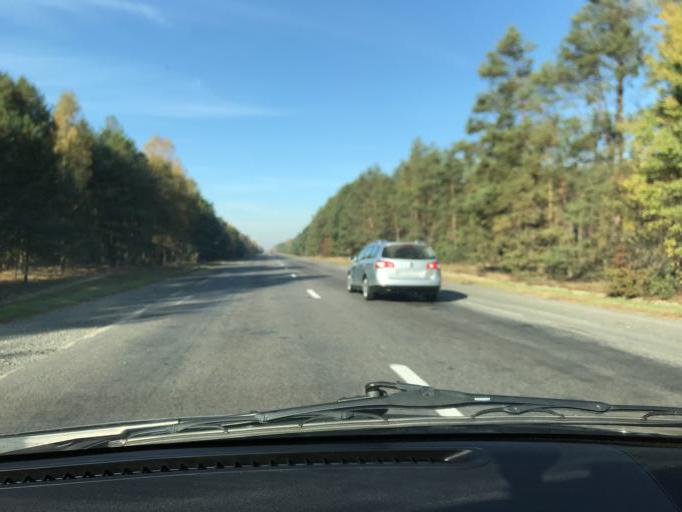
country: BY
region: Brest
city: Luninyets
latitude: 52.2574
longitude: 27.0418
